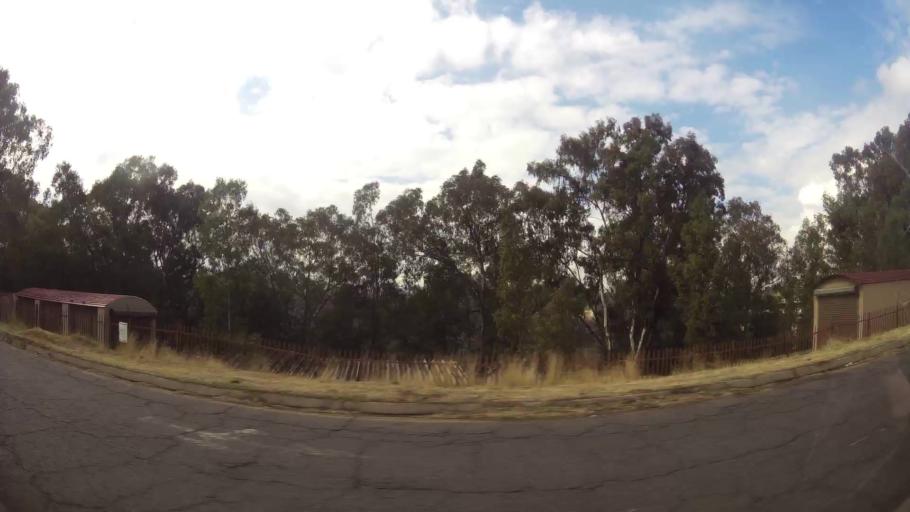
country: ZA
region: Gauteng
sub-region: Sedibeng District Municipality
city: Vereeniging
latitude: -26.6810
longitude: 27.9370
